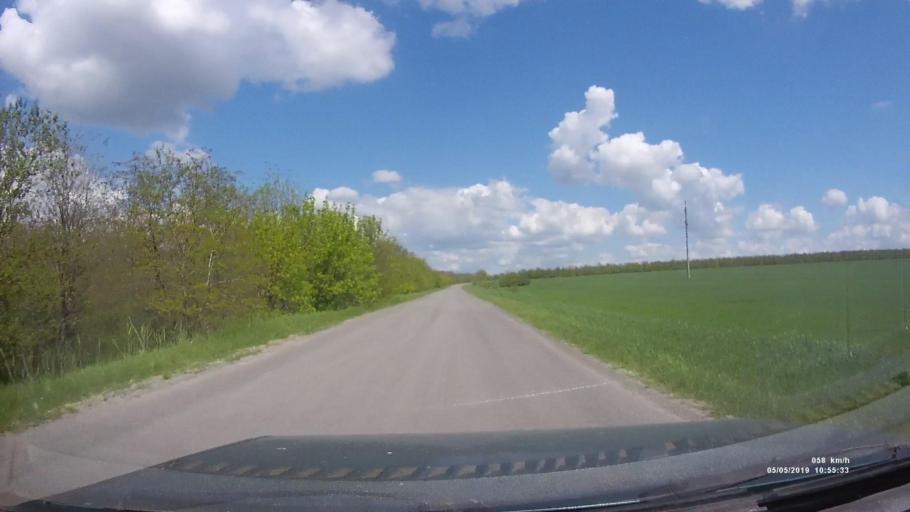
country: RU
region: Rostov
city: Ust'-Donetskiy
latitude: 47.6666
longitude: 40.8207
